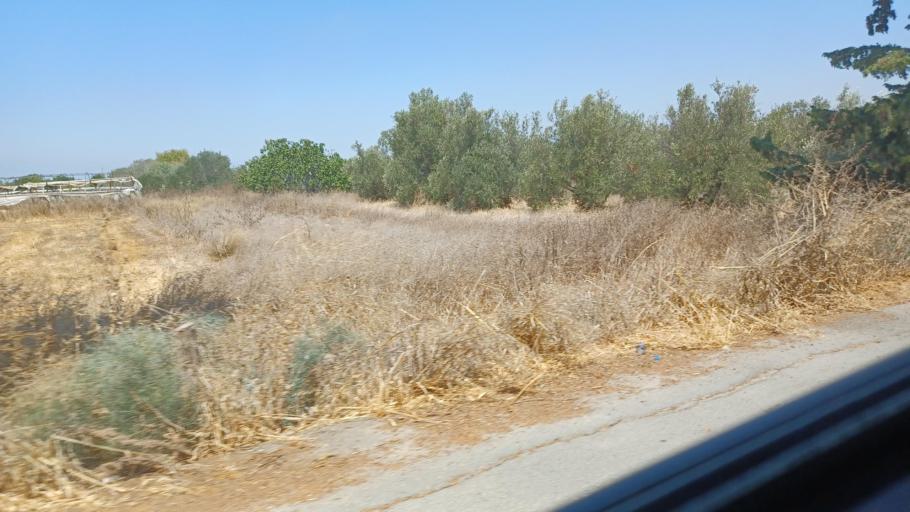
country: CY
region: Pafos
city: Paphos
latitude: 34.7362
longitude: 32.4849
